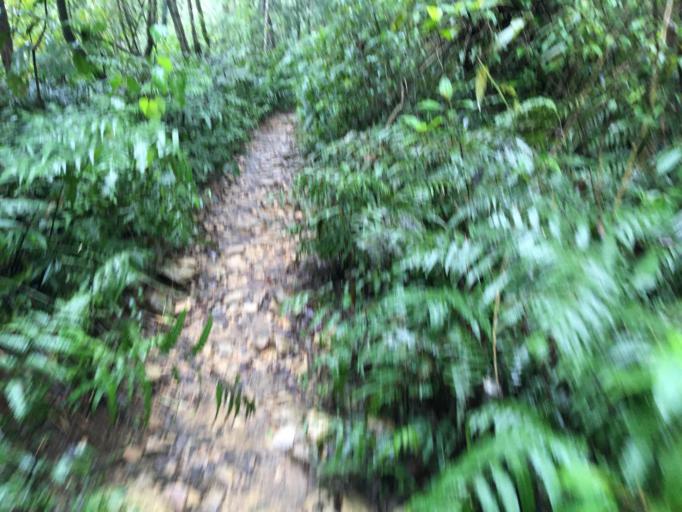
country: TW
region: Taiwan
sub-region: Yilan
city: Yilan
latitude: 24.6770
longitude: 121.5707
